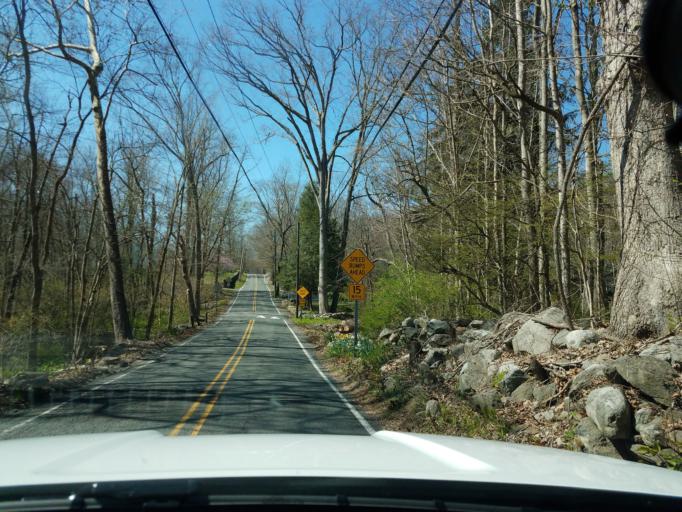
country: US
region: Connecticut
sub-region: Fairfield County
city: Wilton
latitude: 41.2095
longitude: -73.3889
